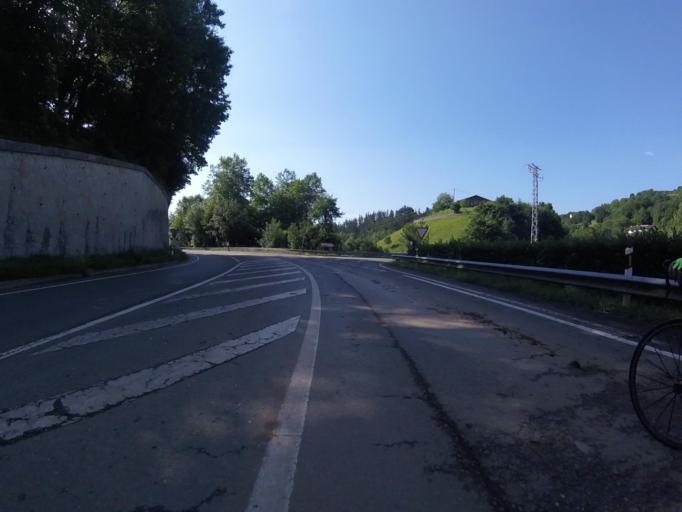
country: ES
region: Basque Country
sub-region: Provincia de Guipuzcoa
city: Asteasu
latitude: 43.1926
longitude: -2.0936
